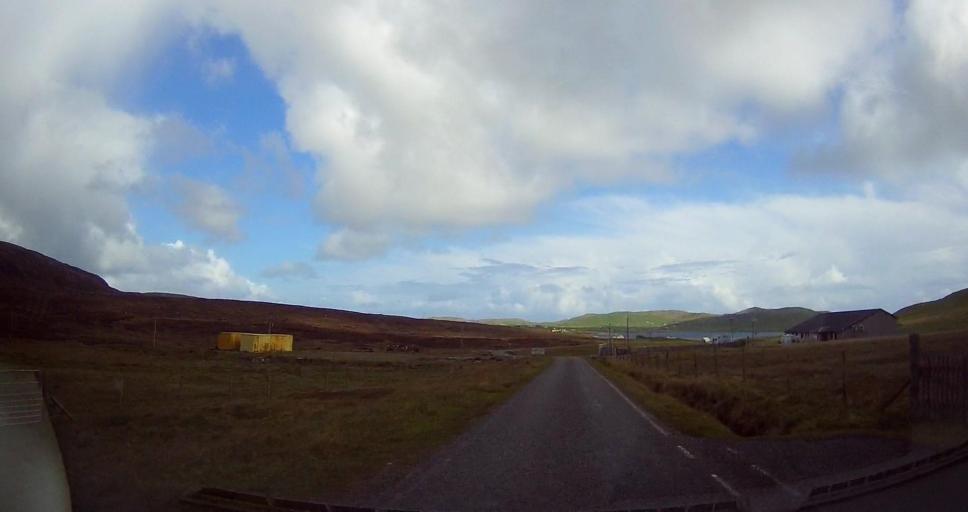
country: GB
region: Scotland
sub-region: Shetland Islands
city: Lerwick
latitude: 60.5712
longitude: -1.3335
